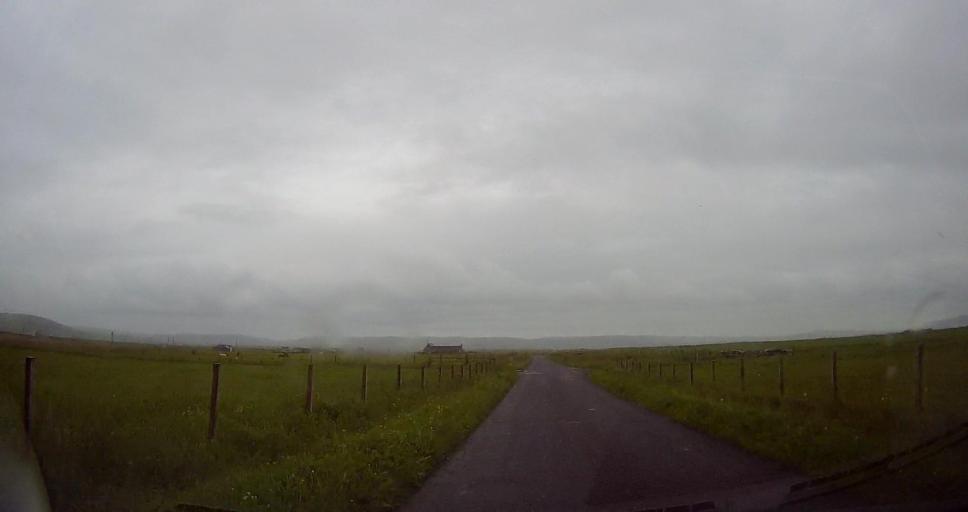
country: GB
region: Scotland
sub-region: Orkney Islands
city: Stromness
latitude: 59.0703
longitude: -3.2878
